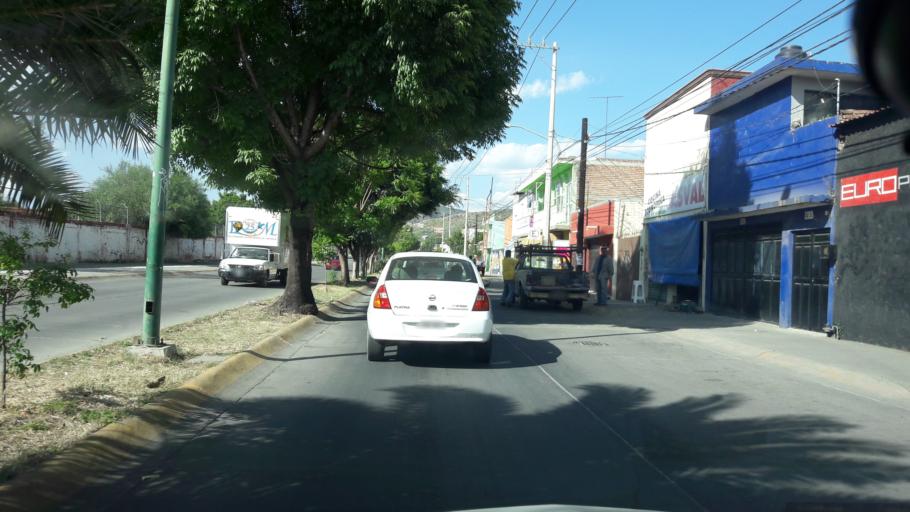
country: MX
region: Guanajuato
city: Leon
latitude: 21.1826
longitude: -101.6669
